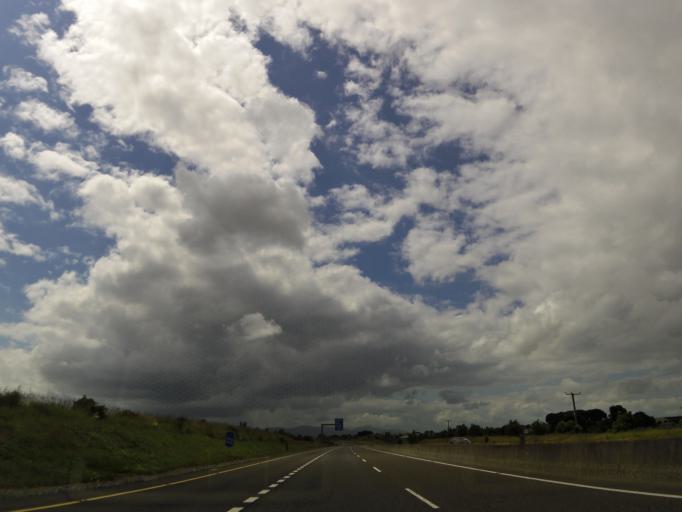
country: IE
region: Munster
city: Cashel
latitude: 52.5043
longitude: -7.8782
